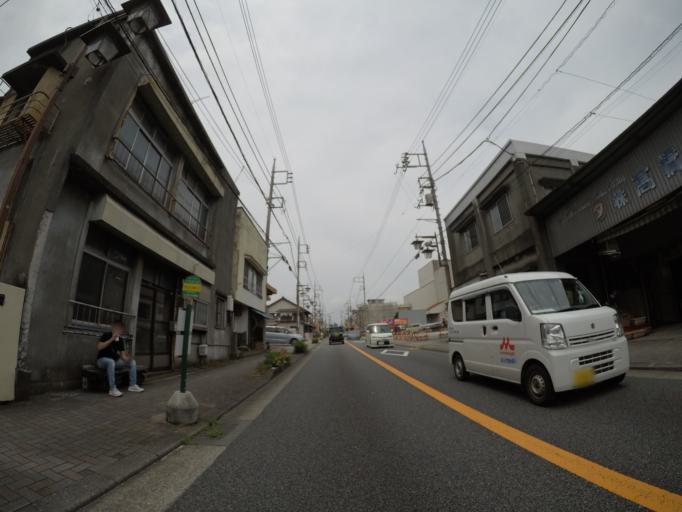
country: JP
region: Shizuoka
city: Fujinomiya
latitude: 35.2267
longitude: 138.6069
